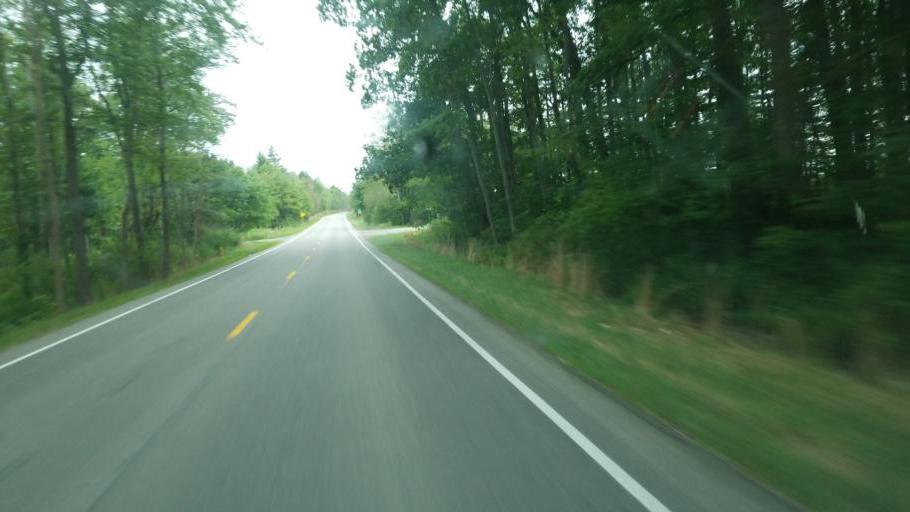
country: US
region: Pennsylvania
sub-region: Clarion County
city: Knox
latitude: 41.2018
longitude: -79.5437
